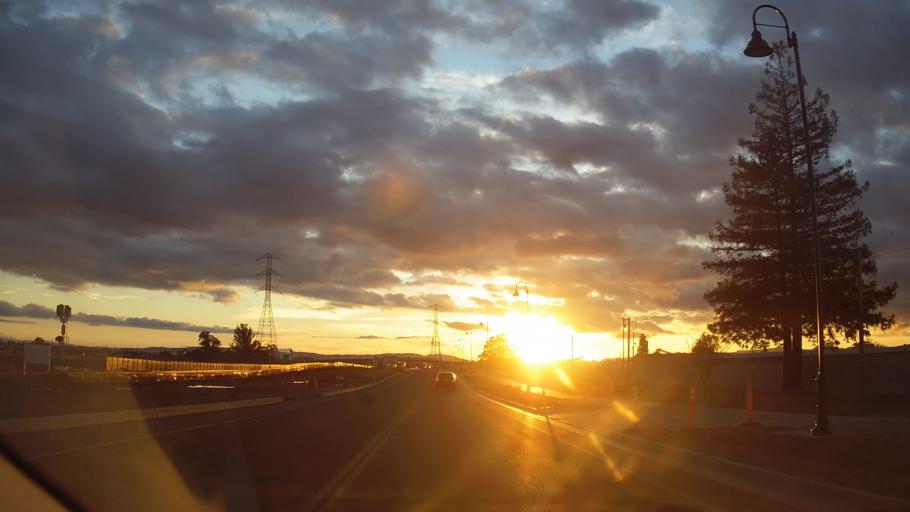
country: US
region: California
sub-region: Solano County
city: Vacaville
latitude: 38.2898
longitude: -121.9610
